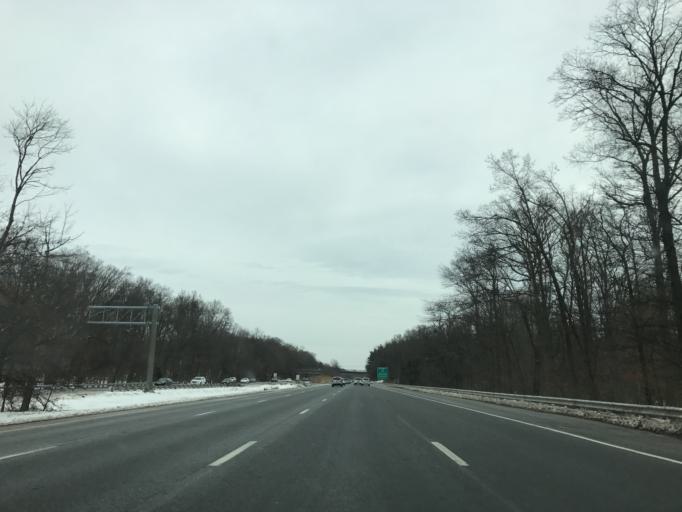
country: US
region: New Jersey
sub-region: Somerset County
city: Bedminster
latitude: 40.6757
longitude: -74.6065
